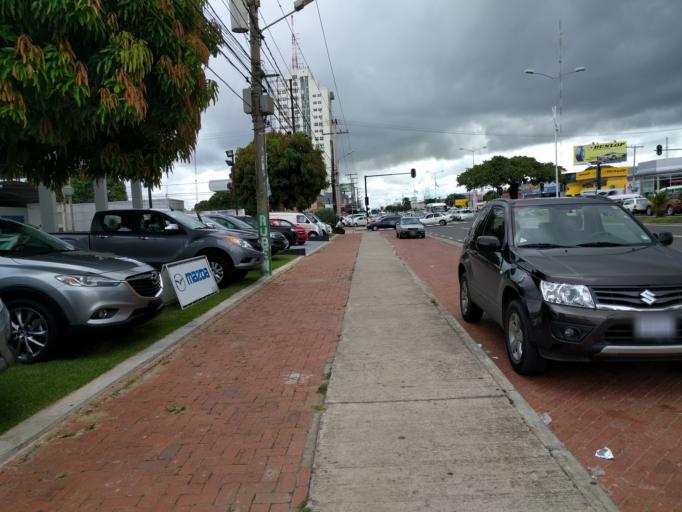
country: BO
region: Santa Cruz
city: Santa Cruz de la Sierra
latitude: -17.7631
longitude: -63.1806
